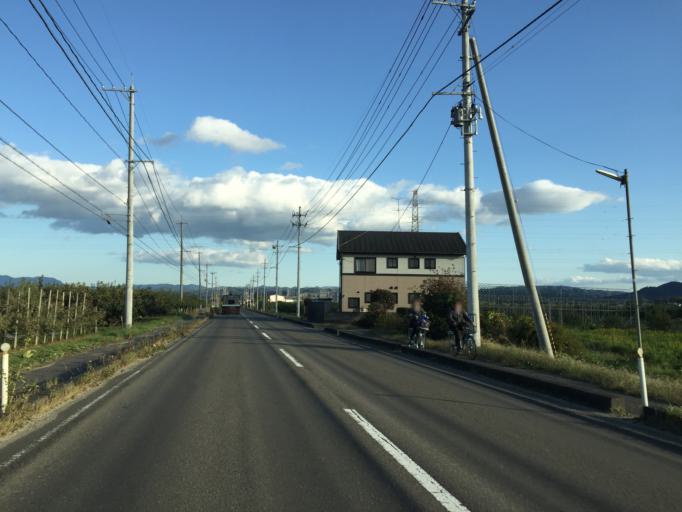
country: JP
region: Fukushima
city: Fukushima-shi
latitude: 37.8171
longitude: 140.4561
